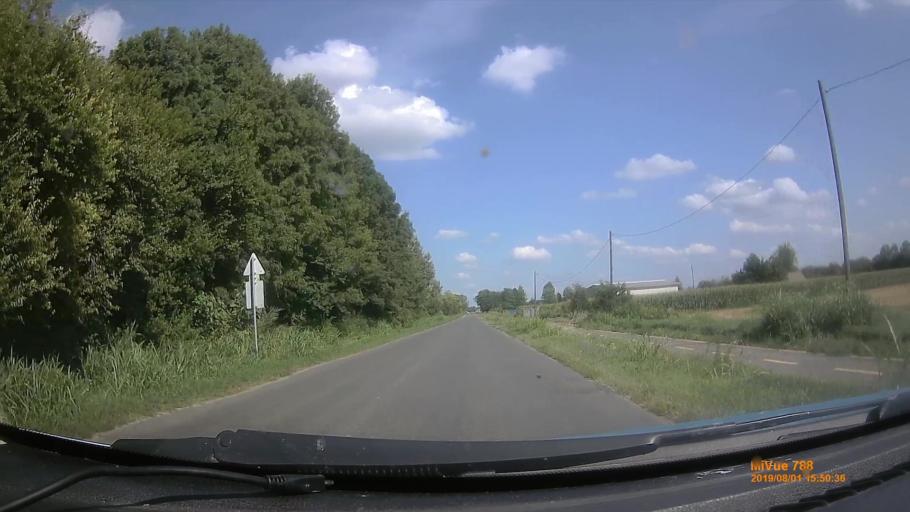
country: HU
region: Baranya
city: Szentlorinc
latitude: 46.0367
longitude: 18.0015
